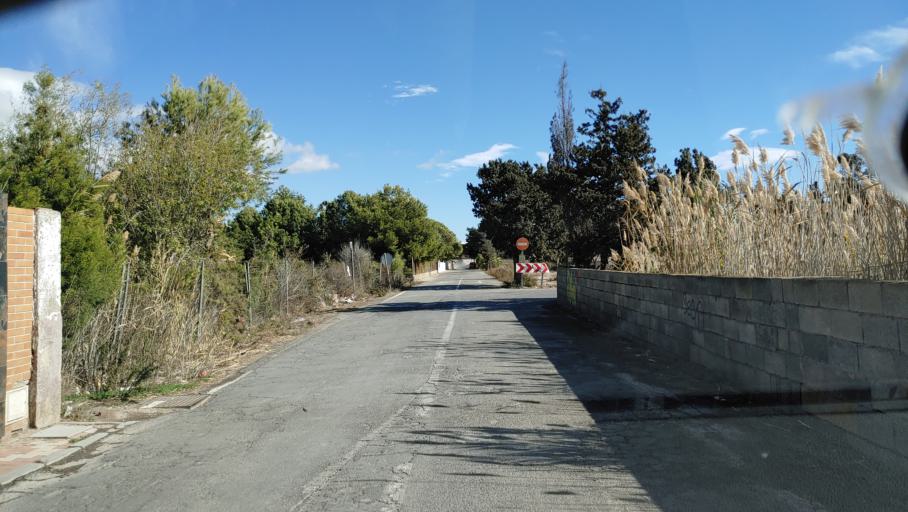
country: ES
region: Andalusia
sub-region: Provincia de Almeria
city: Aguadulce
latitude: 36.7934
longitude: -2.5890
